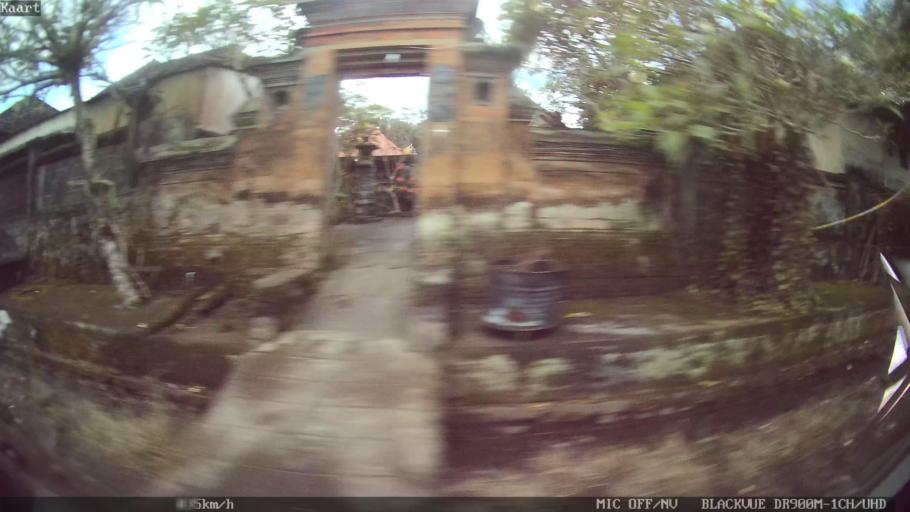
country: ID
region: Bali
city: Banjar Madangan Kaja
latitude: -8.4817
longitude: 115.3214
